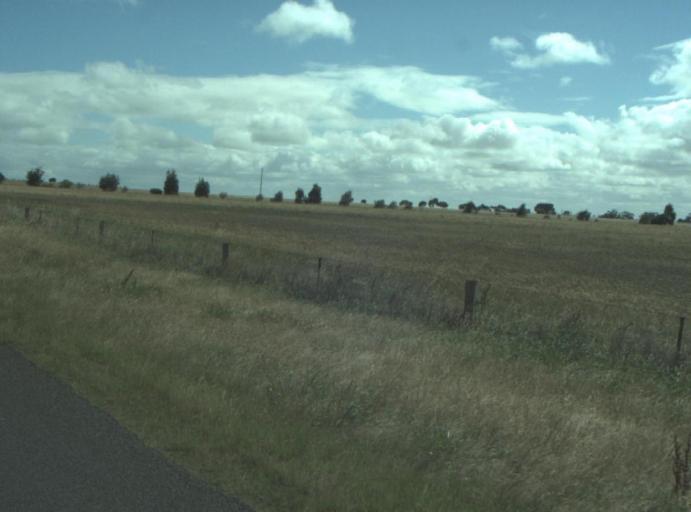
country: AU
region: Victoria
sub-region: Greater Geelong
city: Lara
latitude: -37.8809
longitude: 144.3209
